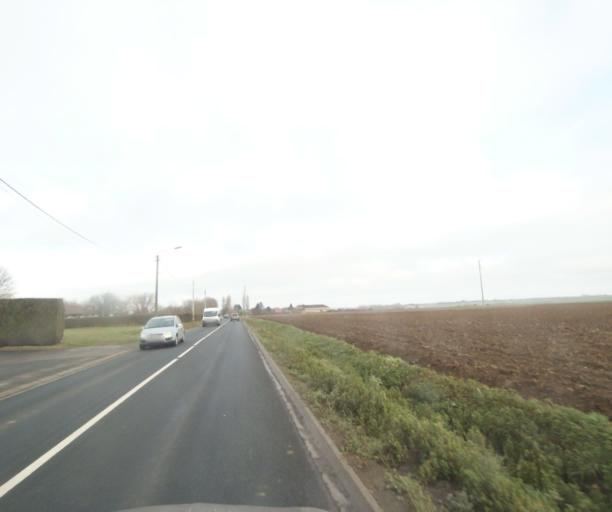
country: FR
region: Nord-Pas-de-Calais
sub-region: Departement du Nord
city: Famars
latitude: 50.3054
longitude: 3.5174
